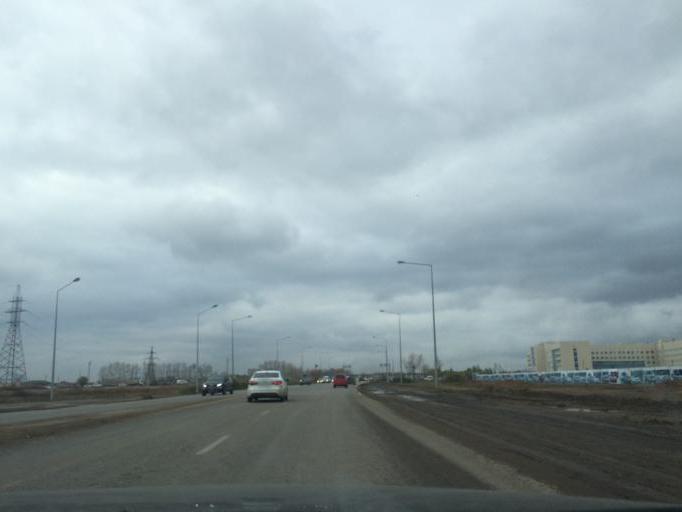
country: KZ
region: Astana Qalasy
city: Astana
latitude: 51.1370
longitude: 71.5328
